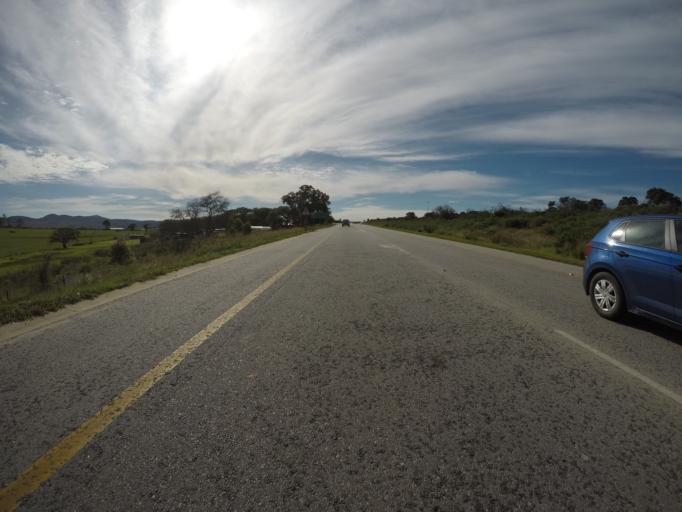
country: ZA
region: Eastern Cape
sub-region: Cacadu District Municipality
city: Jeffrey's Bay
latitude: -33.9001
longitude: 25.1155
